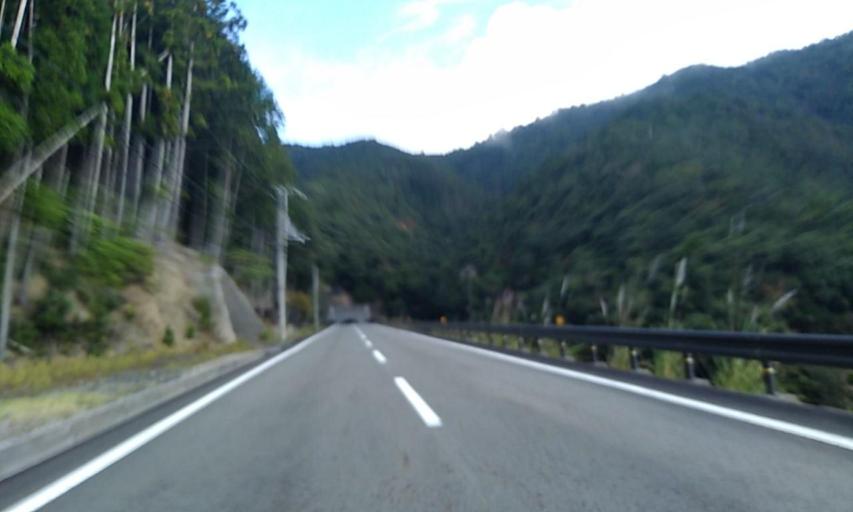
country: JP
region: Wakayama
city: Shingu
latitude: 33.8787
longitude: 135.8763
